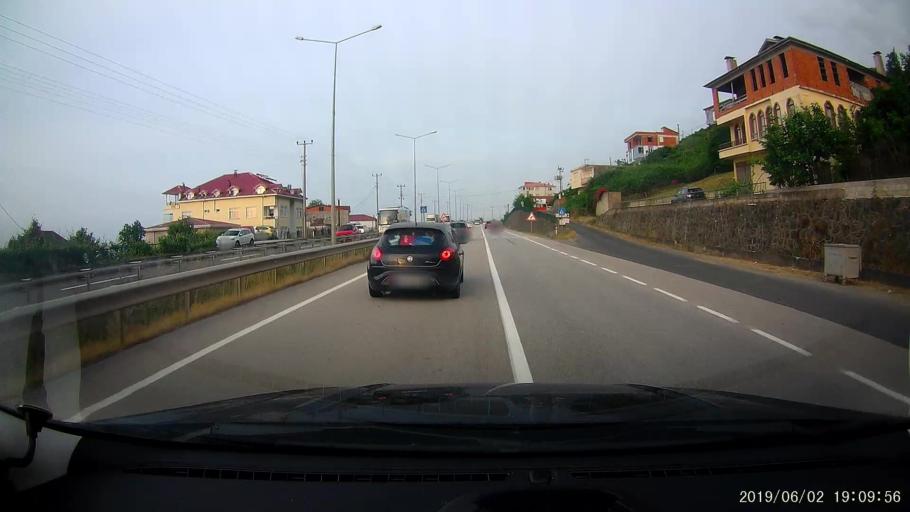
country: TR
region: Ordu
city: Gulyali
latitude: 40.9718
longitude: 38.0365
